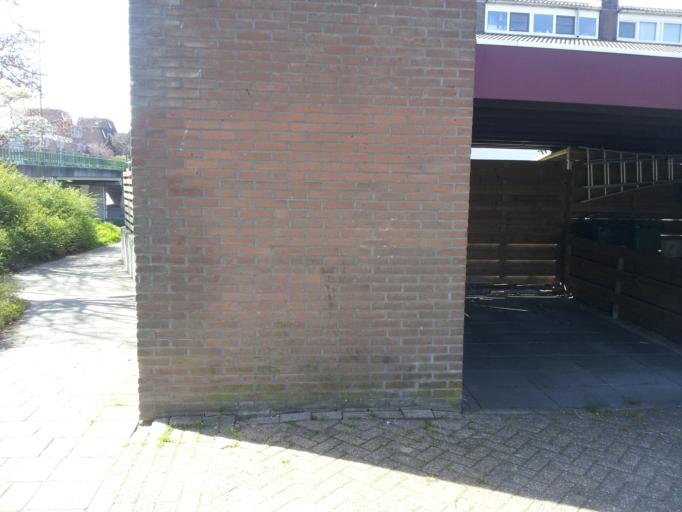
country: NL
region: South Holland
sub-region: Gemeente Zoetermeer
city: Zoetermeer
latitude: 52.0731
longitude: 4.4963
